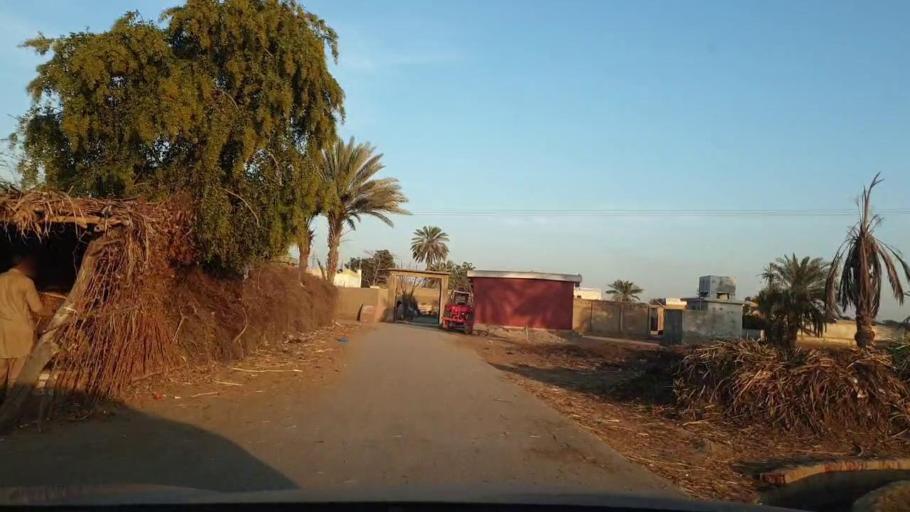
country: PK
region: Sindh
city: Tando Adam
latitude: 25.6196
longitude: 68.6898
